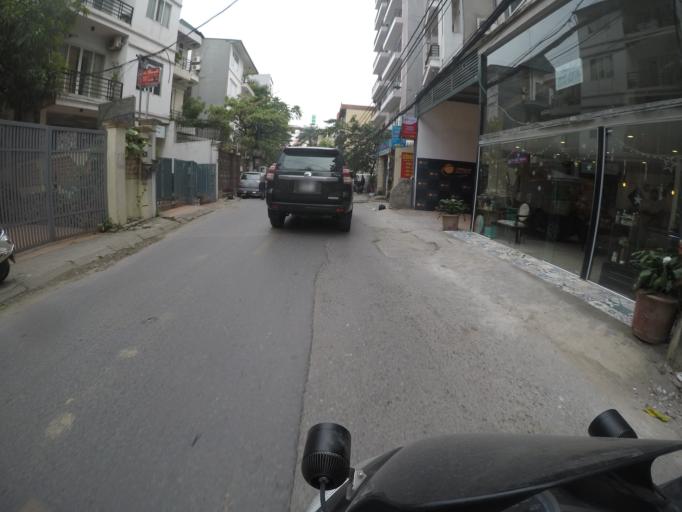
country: VN
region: Ha Noi
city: Tay Ho
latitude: 21.0685
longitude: 105.8245
